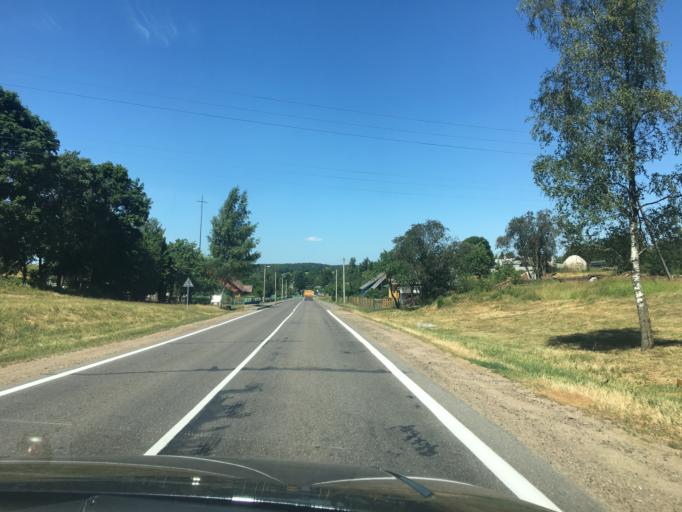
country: BY
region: Grodnenskaya
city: Hal'shany
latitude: 54.1521
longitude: 25.9113
